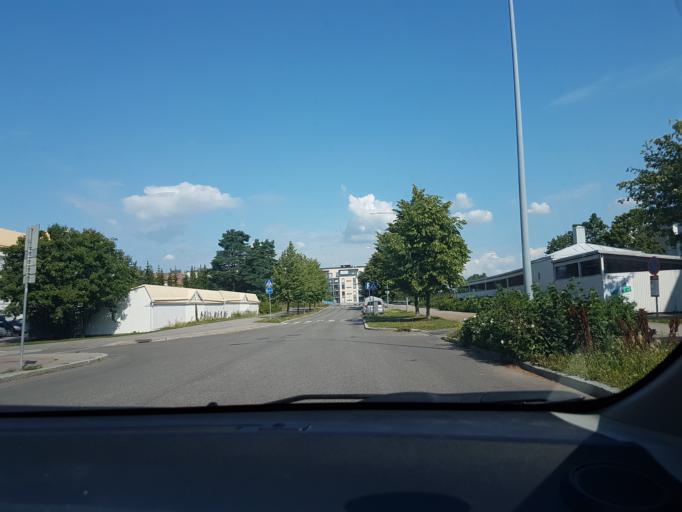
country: FI
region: Uusimaa
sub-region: Helsinki
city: Vantaa
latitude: 60.2032
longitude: 25.1274
